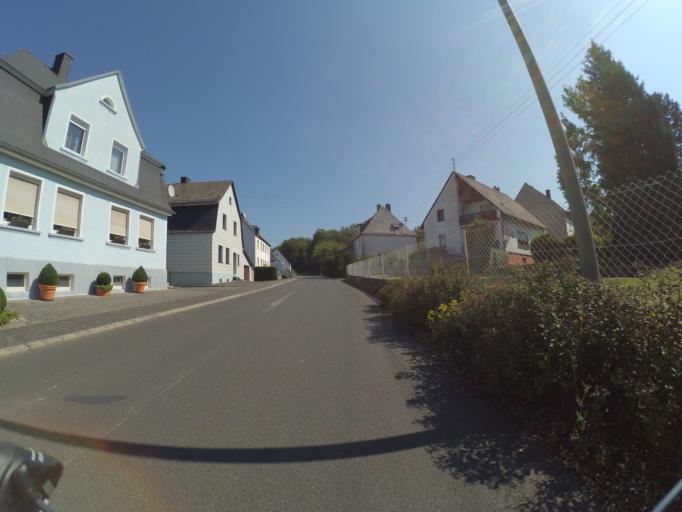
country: DE
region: Rheinland-Pfalz
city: Rorodt
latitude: 49.7731
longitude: 7.0968
